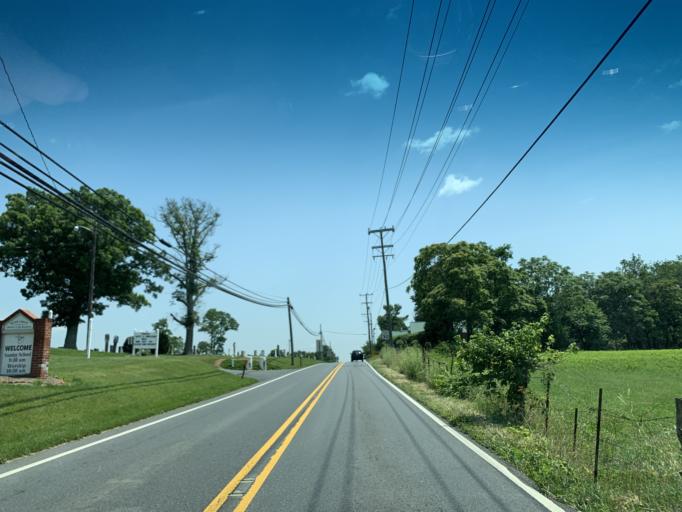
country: US
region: Maryland
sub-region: Frederick County
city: Green Valley
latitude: 39.3660
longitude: -77.2705
